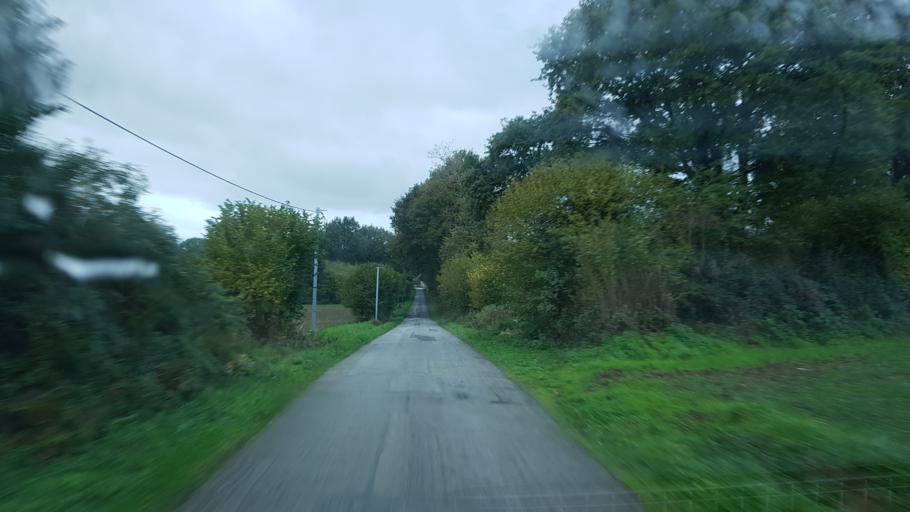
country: FR
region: Brittany
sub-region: Departement du Morbihan
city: Elven
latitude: 47.7455
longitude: -2.5601
